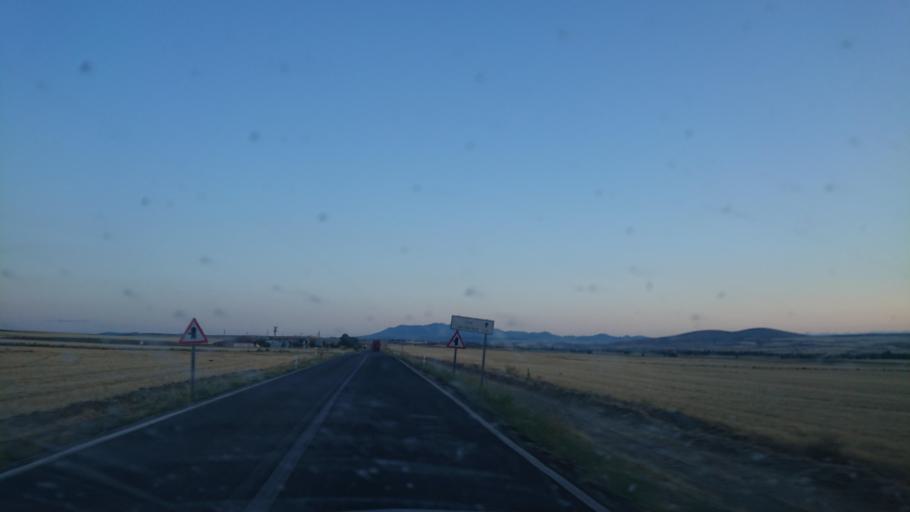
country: TR
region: Aksaray
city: Balci
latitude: 38.8263
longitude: 34.1372
